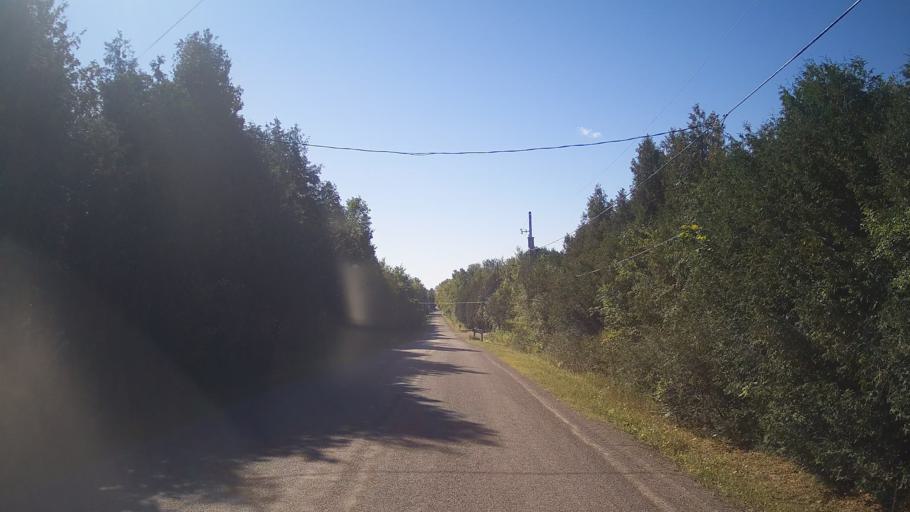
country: CA
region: Ontario
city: Prescott
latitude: 44.9880
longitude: -75.5852
